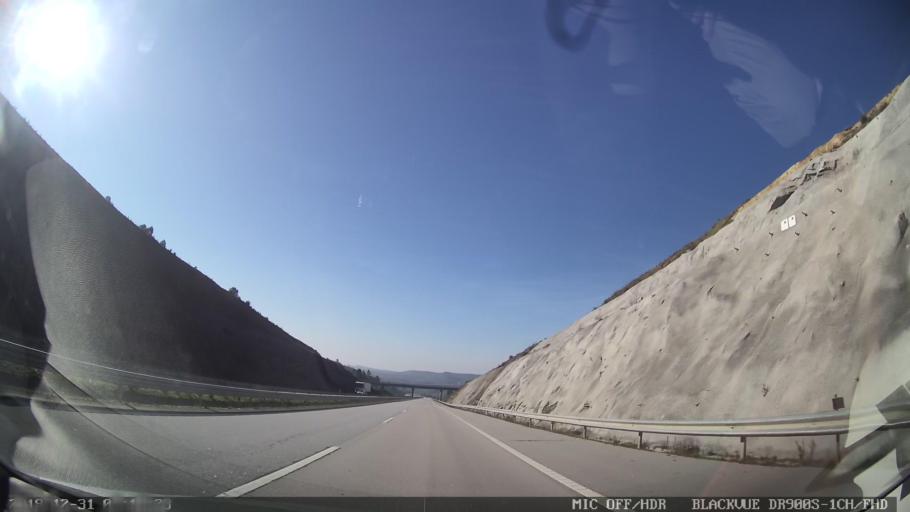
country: PT
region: Portalegre
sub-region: Gaviao
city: Gaviao
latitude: 39.5432
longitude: -7.8812
